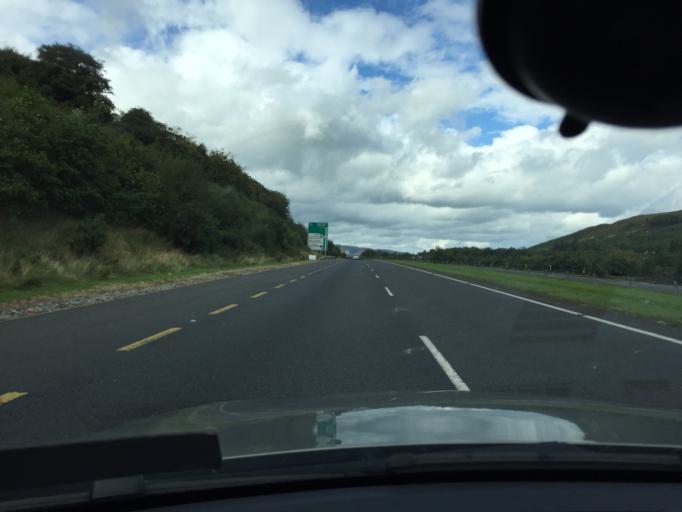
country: GB
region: Northern Ireland
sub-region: Newry and Mourne District
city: Newry
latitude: 54.0866
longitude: -6.3579
